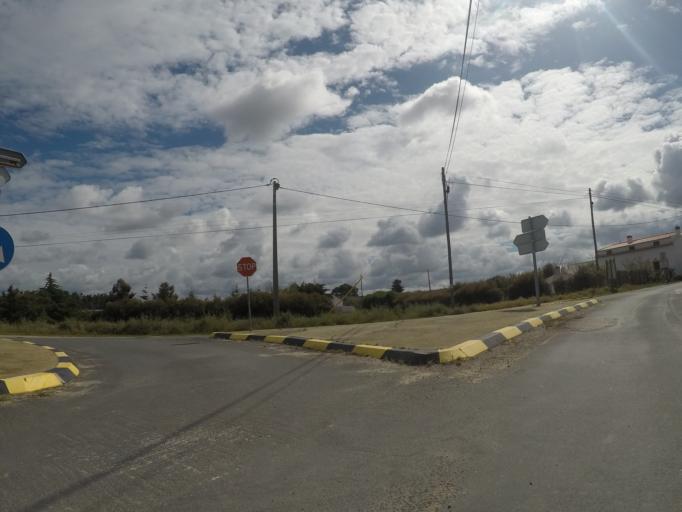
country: PT
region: Beja
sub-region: Odemira
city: Sao Teotonio
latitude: 37.4812
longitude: -8.7679
